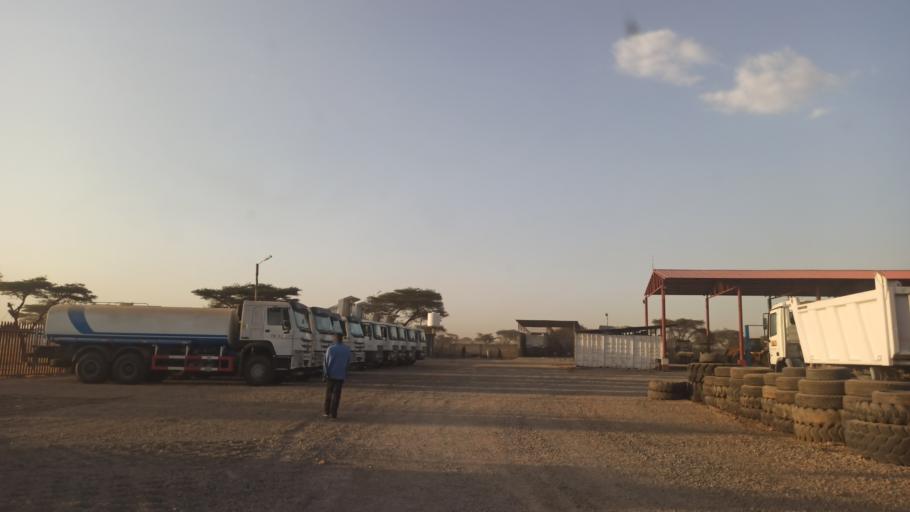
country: ET
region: Oromiya
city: Ziway
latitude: 7.7026
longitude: 38.6529
